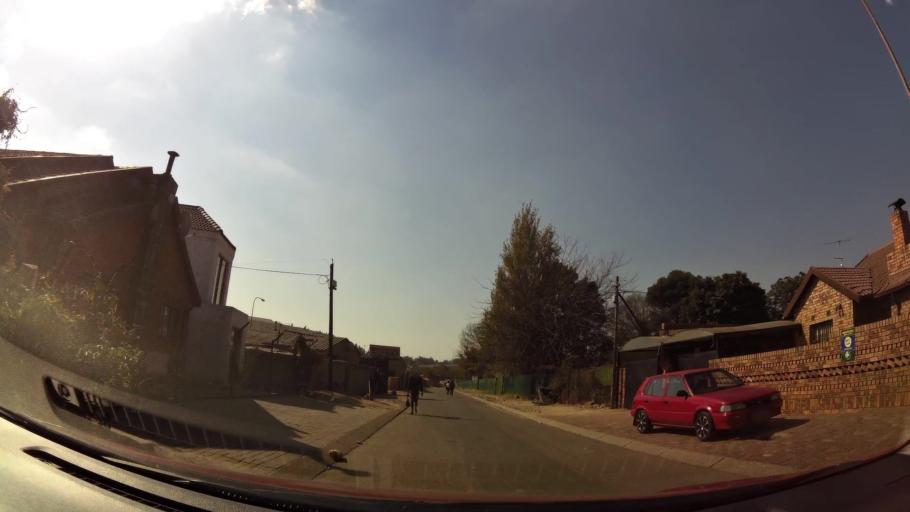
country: ZA
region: Gauteng
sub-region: City of Johannesburg Metropolitan Municipality
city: Johannesburg
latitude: -26.2377
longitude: 27.9530
